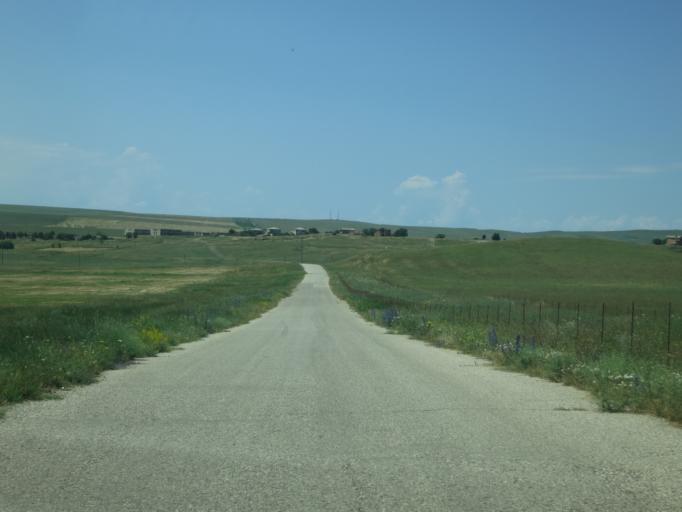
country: GE
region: Kakheti
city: Sagarejo
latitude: 41.5100
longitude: 45.3903
